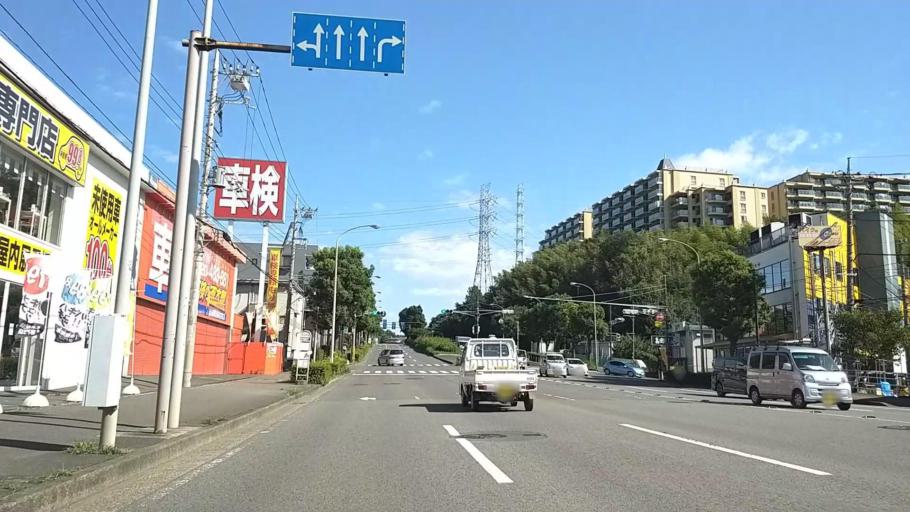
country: JP
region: Kanagawa
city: Yokohama
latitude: 35.5301
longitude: 139.5926
